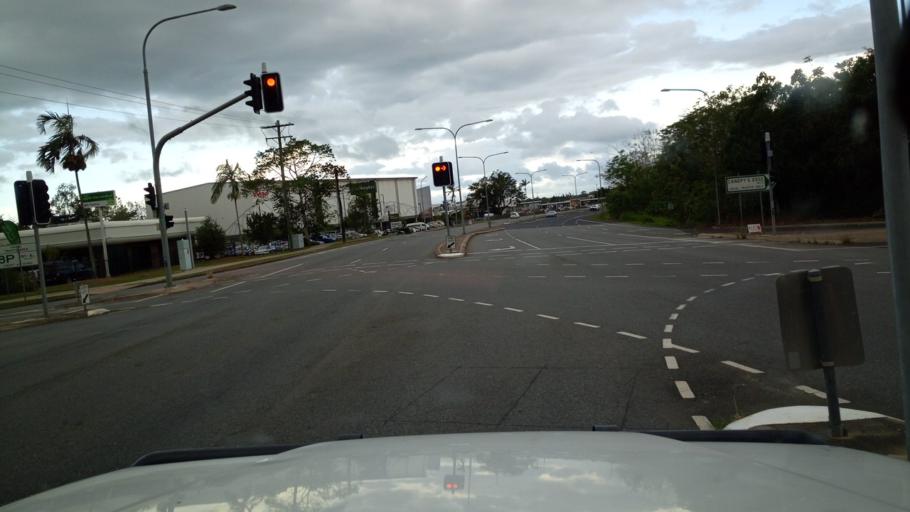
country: AU
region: Queensland
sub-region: Cairns
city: Redlynch
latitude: -16.8389
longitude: 145.6896
